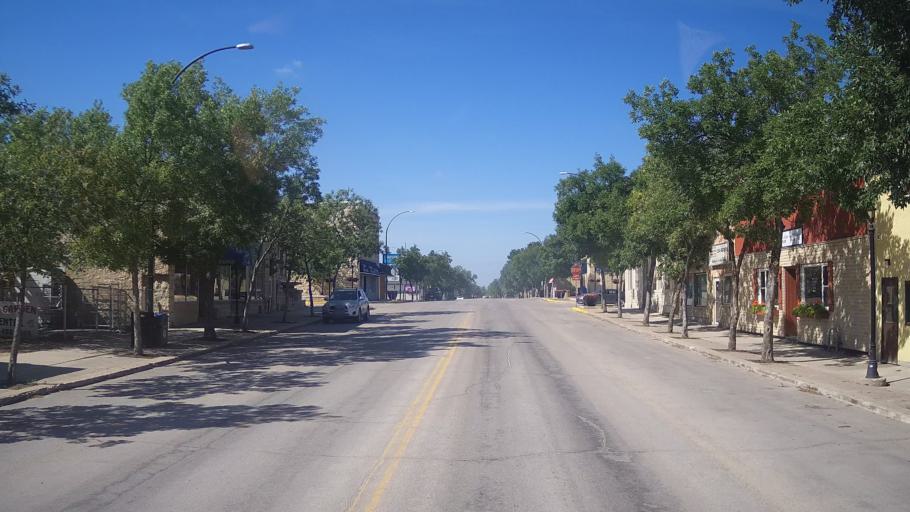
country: CA
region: Manitoba
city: Stonewall
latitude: 50.1341
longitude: -97.3267
